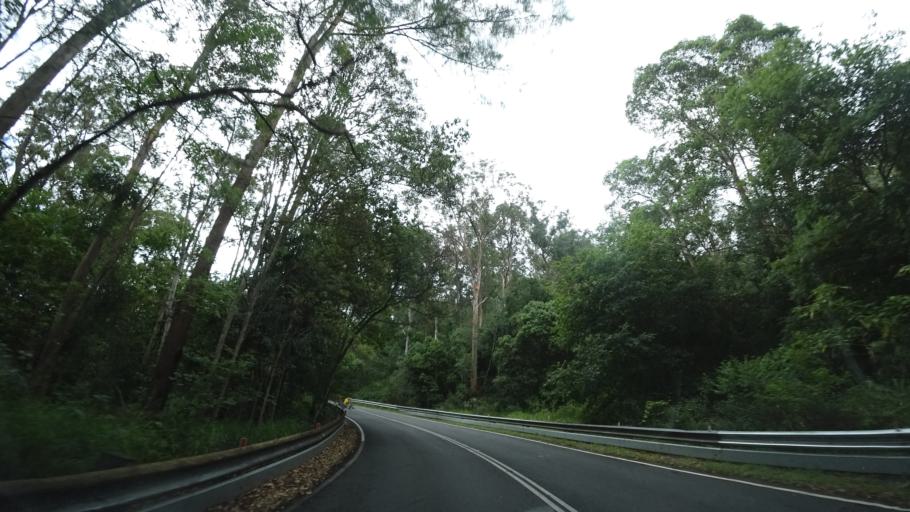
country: AU
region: Queensland
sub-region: Brisbane
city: Taringa
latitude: -27.4639
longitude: 152.9622
